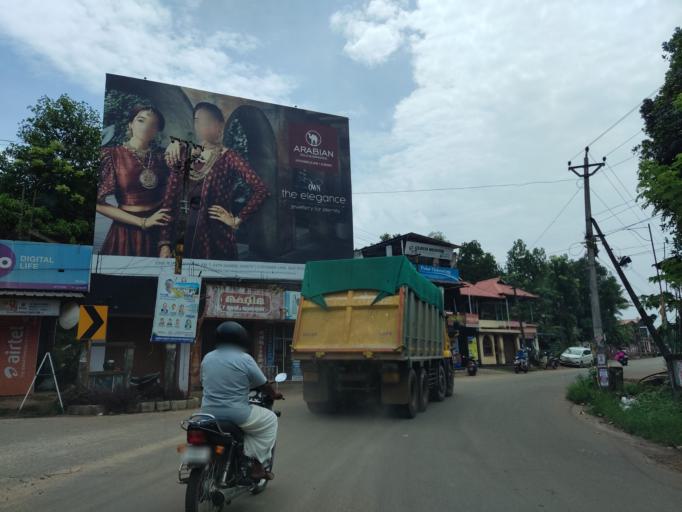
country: IN
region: Kerala
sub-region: Alappuzha
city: Mavelikara
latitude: 9.2271
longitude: 76.6114
